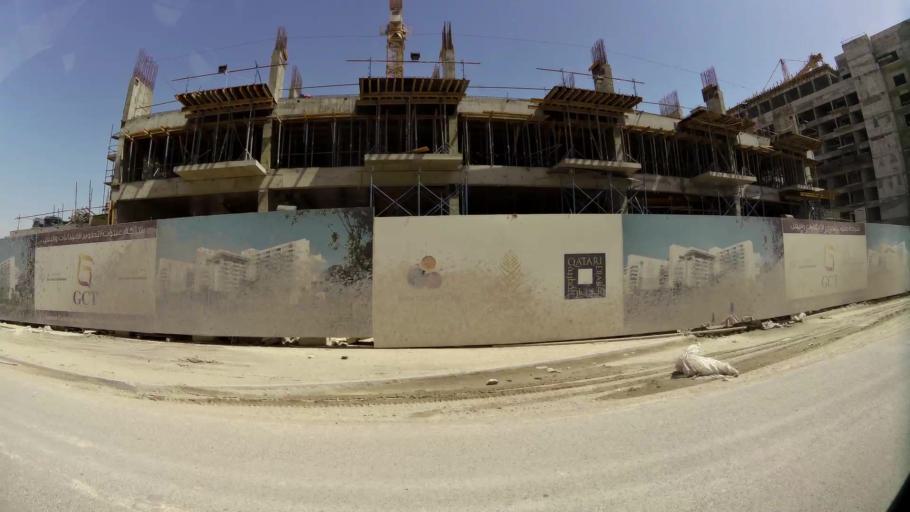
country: QA
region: Baladiyat Umm Salal
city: Umm Salal Muhammad
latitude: 25.4062
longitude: 51.5211
